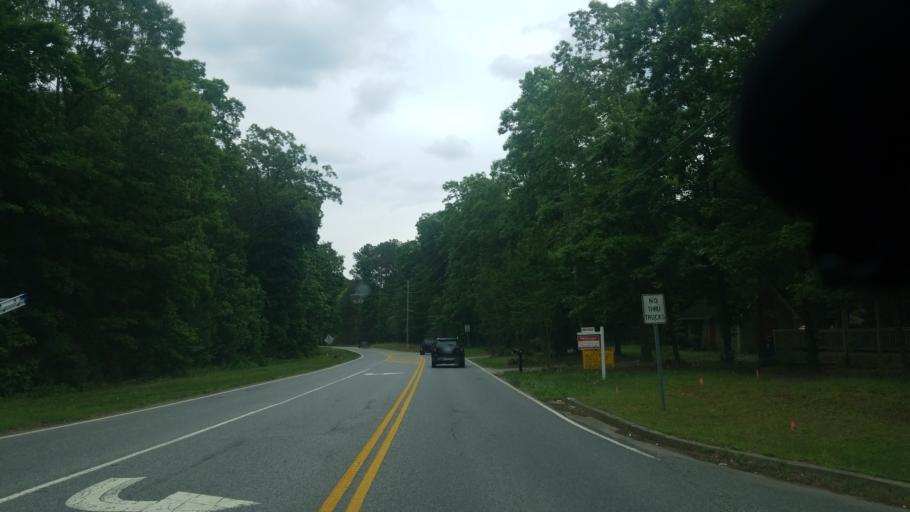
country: US
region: Georgia
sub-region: Forsyth County
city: Cumming
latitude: 34.1716
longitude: -84.1343
